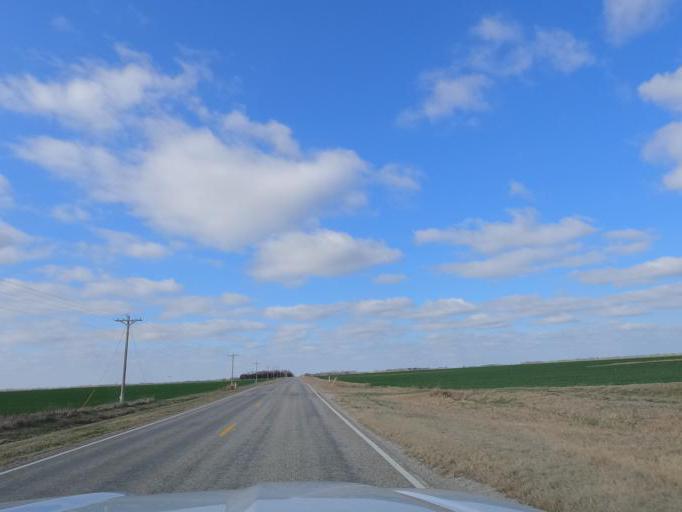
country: US
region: Kansas
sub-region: McPherson County
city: Inman
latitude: 38.1955
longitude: -97.8486
